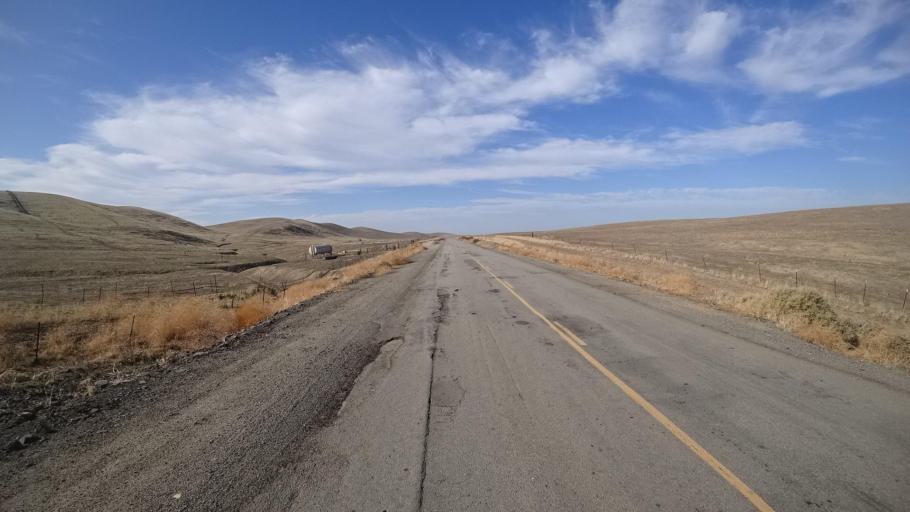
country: US
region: California
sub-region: Tulare County
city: Richgrove
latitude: 35.6246
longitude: -119.0011
